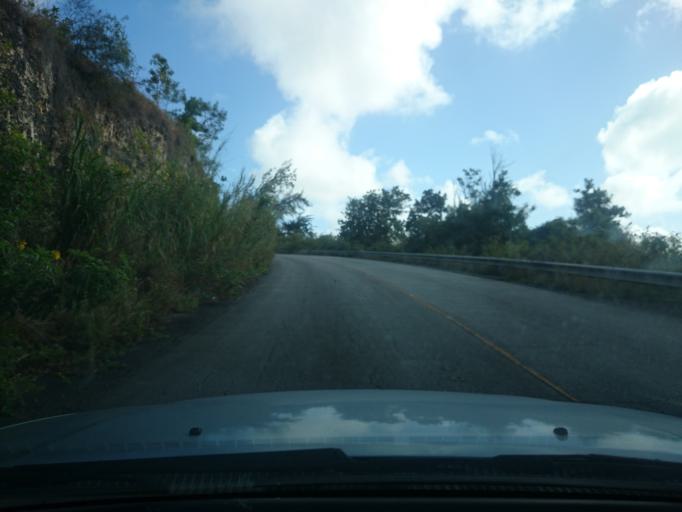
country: BB
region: Saint Lucy
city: Checker Hall
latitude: 13.2747
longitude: -59.6193
